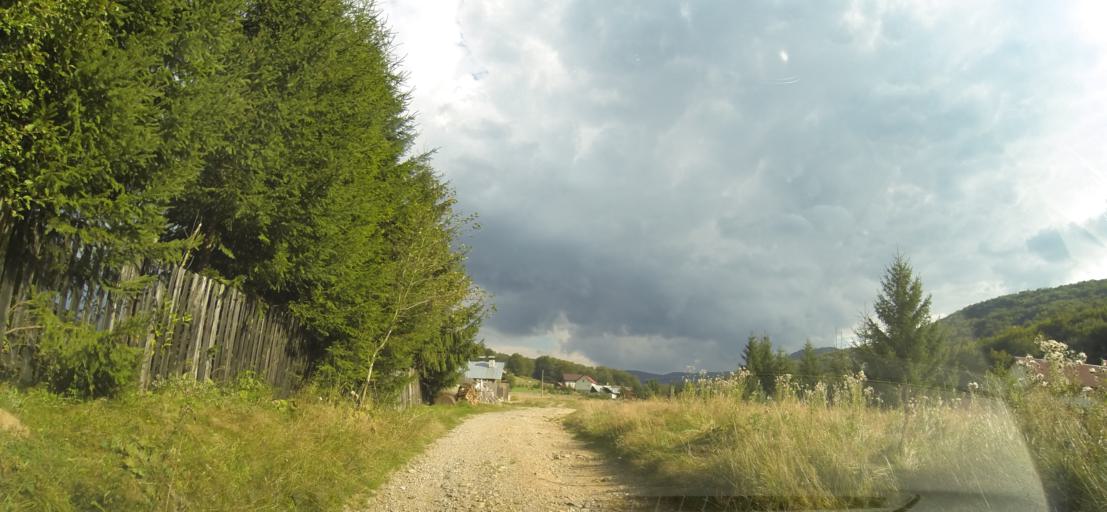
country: RO
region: Brasov
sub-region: Comuna Tarlungeni
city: Zizin
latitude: 45.5142
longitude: 25.8459
